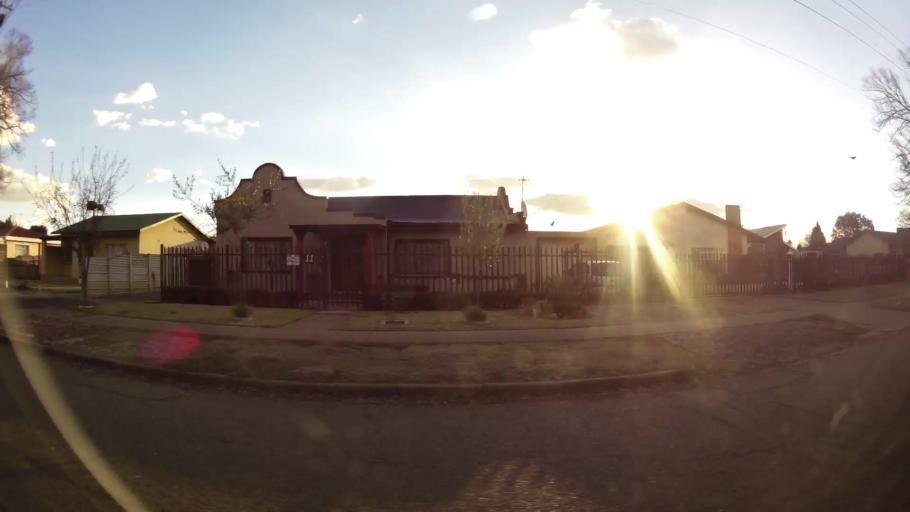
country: ZA
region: North-West
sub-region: Dr Kenneth Kaunda District Municipality
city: Potchefstroom
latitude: -26.7318
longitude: 27.0912
